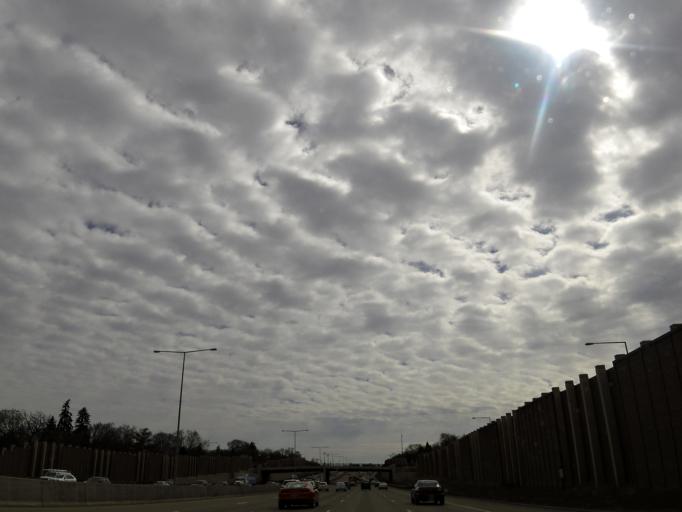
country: US
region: Minnesota
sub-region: Hennepin County
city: Richfield
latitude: 44.9060
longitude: -93.2751
